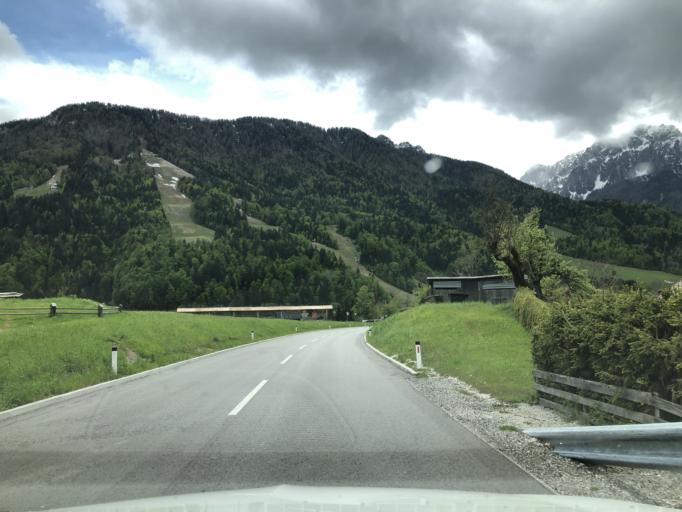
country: SI
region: Kranjska Gora
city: Kranjska Gora
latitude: 46.4966
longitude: 13.7593
